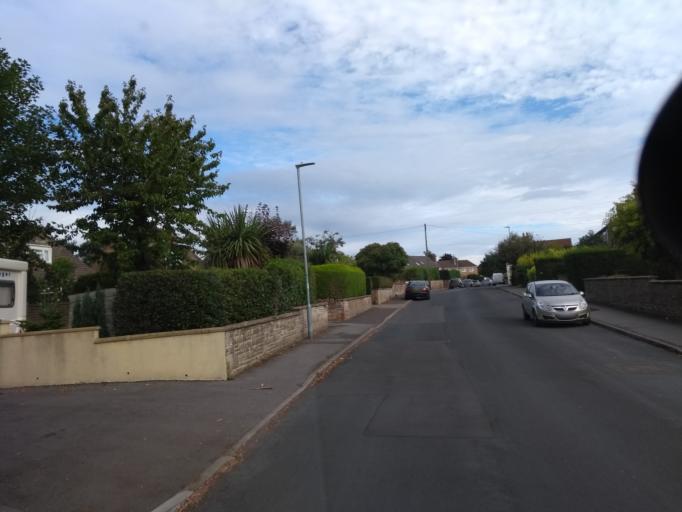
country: GB
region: England
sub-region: Somerset
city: Crewkerne
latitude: 50.8766
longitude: -2.7968
